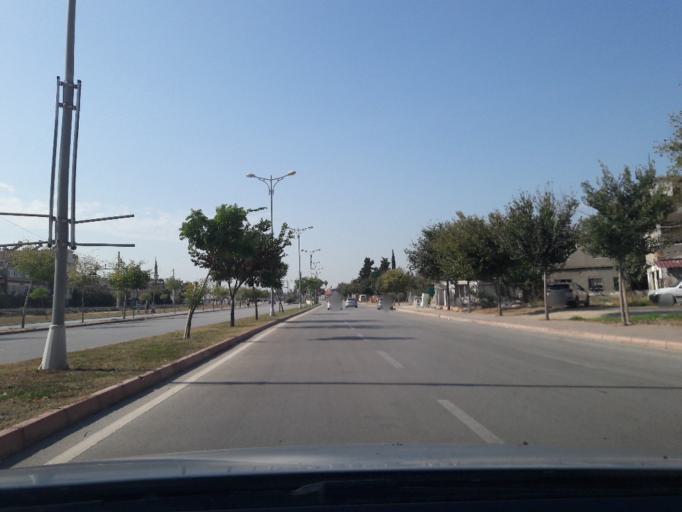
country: TR
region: Adana
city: Seyhan
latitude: 36.9993
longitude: 35.3045
